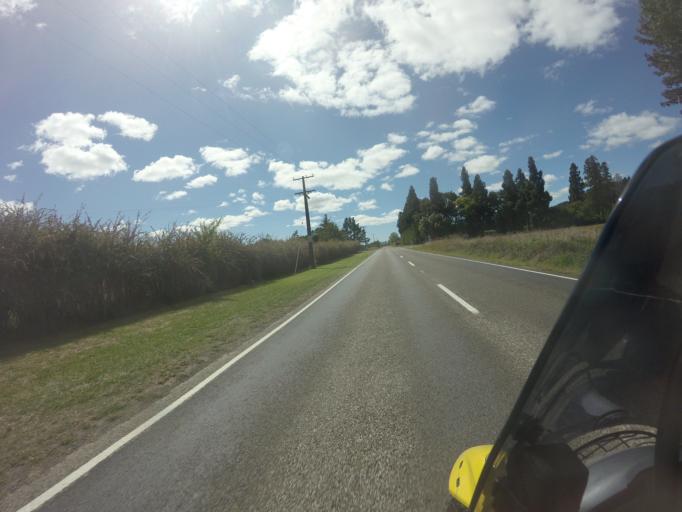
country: NZ
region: Bay of Plenty
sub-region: Whakatane District
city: Edgecumbe
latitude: -38.0600
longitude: 176.8240
